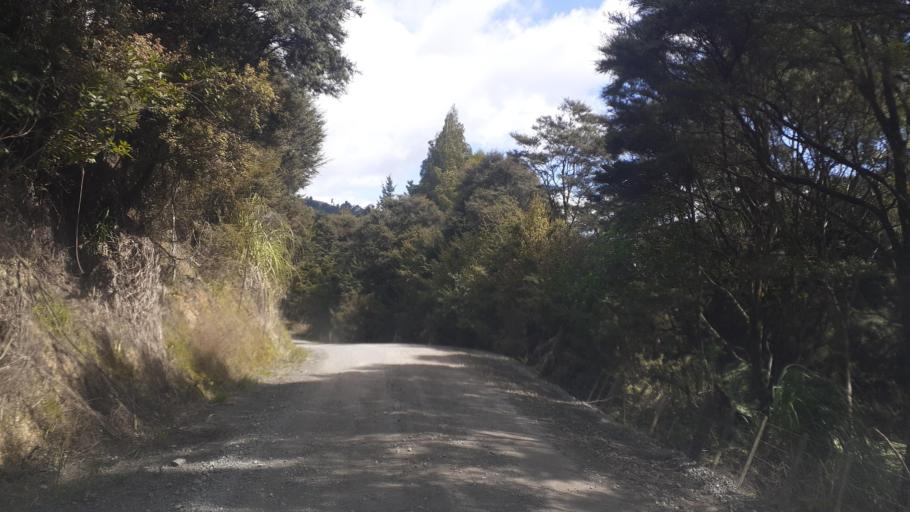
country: NZ
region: Northland
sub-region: Far North District
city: Moerewa
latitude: -35.5787
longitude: 173.9456
